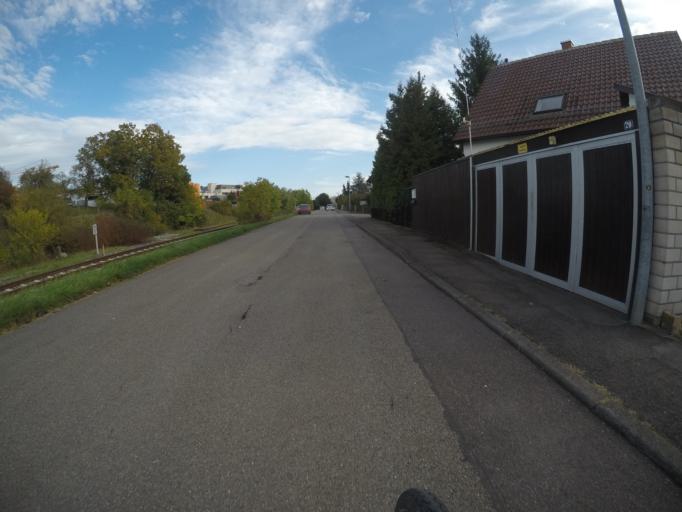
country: DE
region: Baden-Wuerttemberg
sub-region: Regierungsbezirk Stuttgart
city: Herrenberg
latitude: 48.5761
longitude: 8.8847
